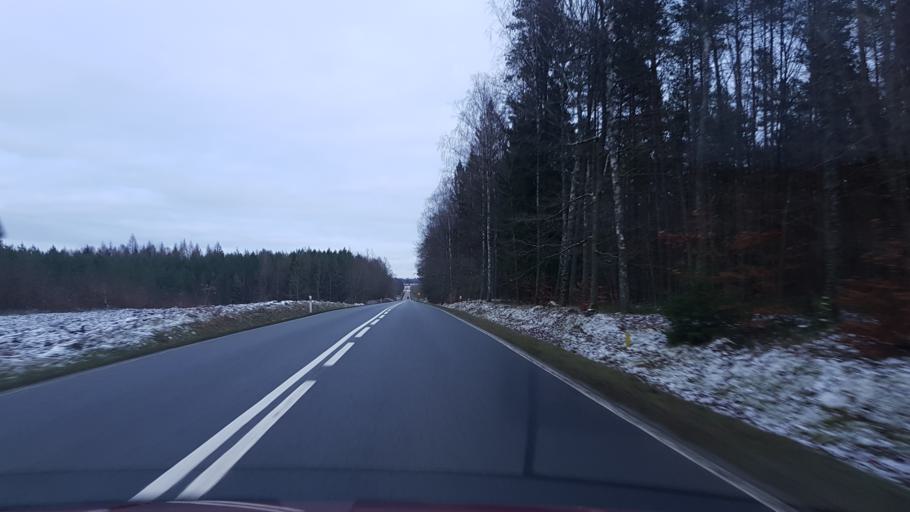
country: PL
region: Pomeranian Voivodeship
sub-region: Powiat czluchowski
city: Koczala
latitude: 54.0178
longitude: 17.1355
